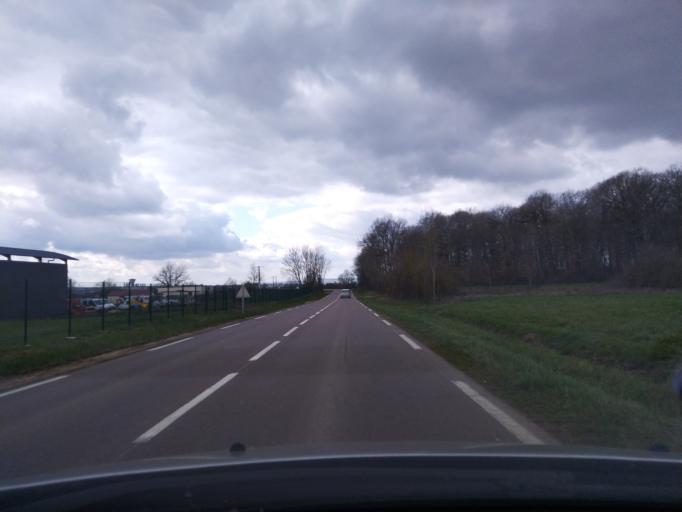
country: FR
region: Bourgogne
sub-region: Departement de l'Yonne
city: Avallon
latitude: 47.5074
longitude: 3.9333
